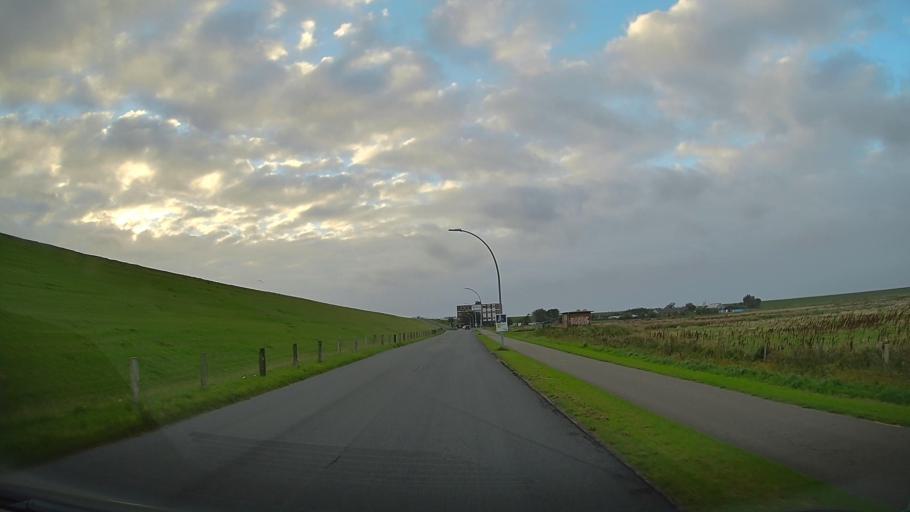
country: DE
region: Schleswig-Holstein
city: Schobull
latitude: 54.4765
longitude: 9.0149
